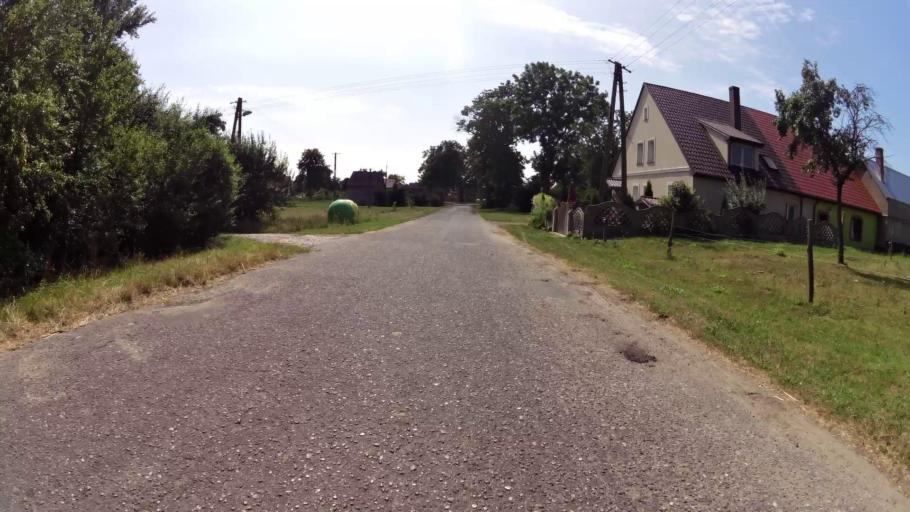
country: PL
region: West Pomeranian Voivodeship
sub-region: Powiat stargardzki
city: Suchan
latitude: 53.2701
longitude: 15.4079
